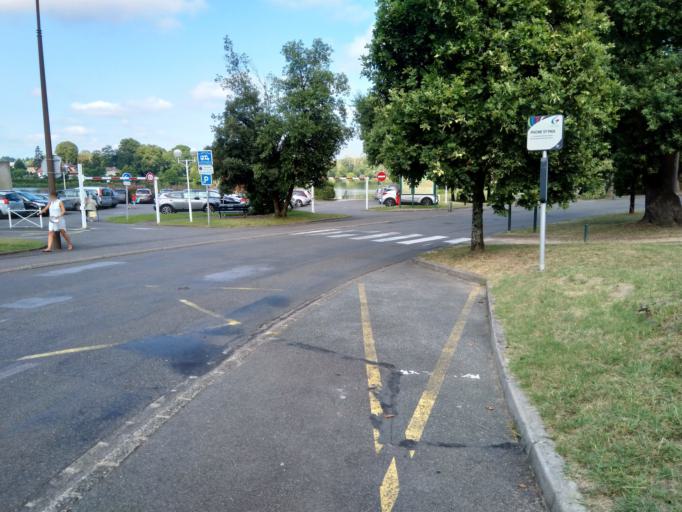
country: FR
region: Aquitaine
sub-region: Departement des Landes
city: Saint-Paul-les-Dax
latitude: 43.7276
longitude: -1.0640
